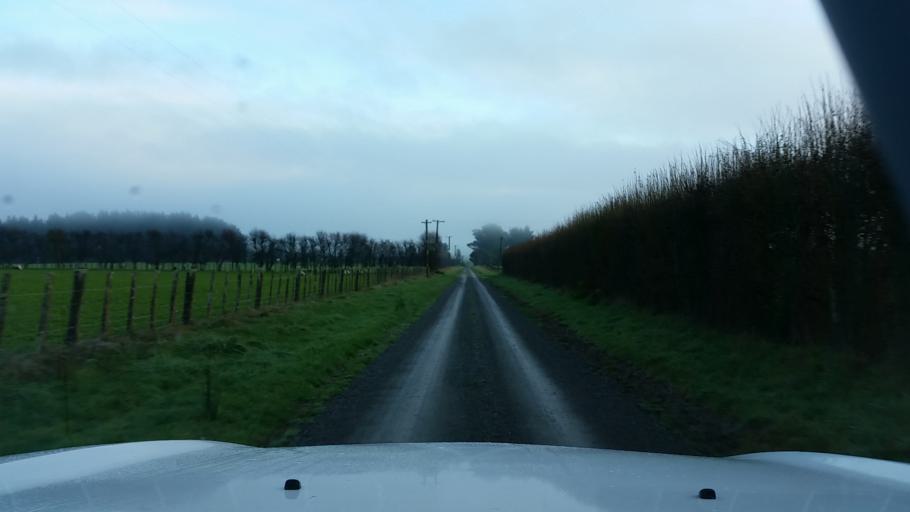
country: NZ
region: Wellington
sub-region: Masterton District
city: Masterton
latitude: -41.0818
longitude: 175.6619
